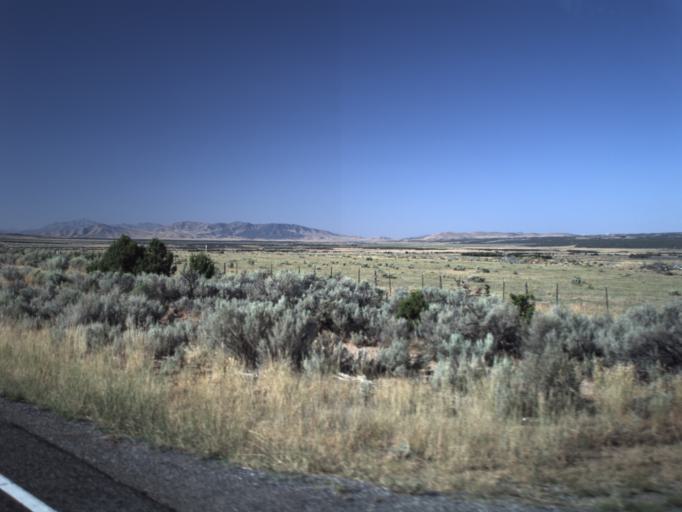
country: US
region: Utah
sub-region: Juab County
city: Mona
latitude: 39.9075
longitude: -112.1400
